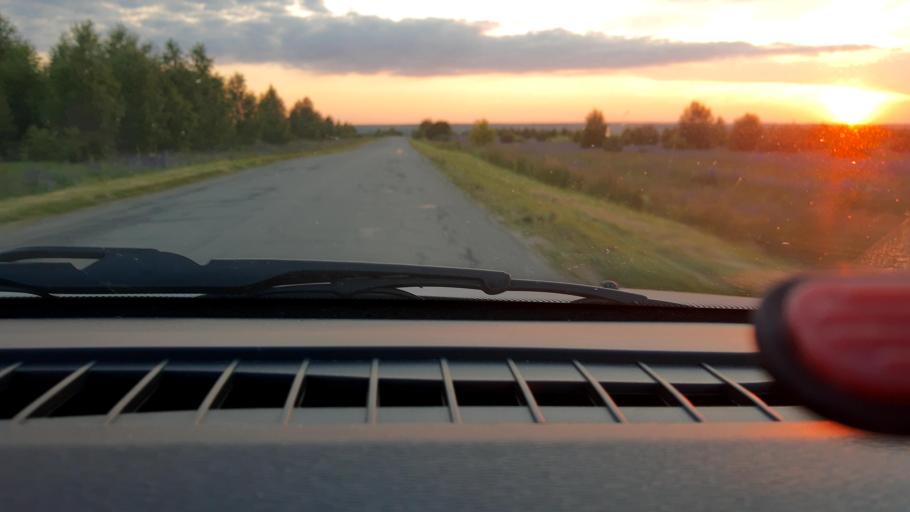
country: RU
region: Nizjnij Novgorod
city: Surovatikha
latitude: 55.8488
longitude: 43.9547
